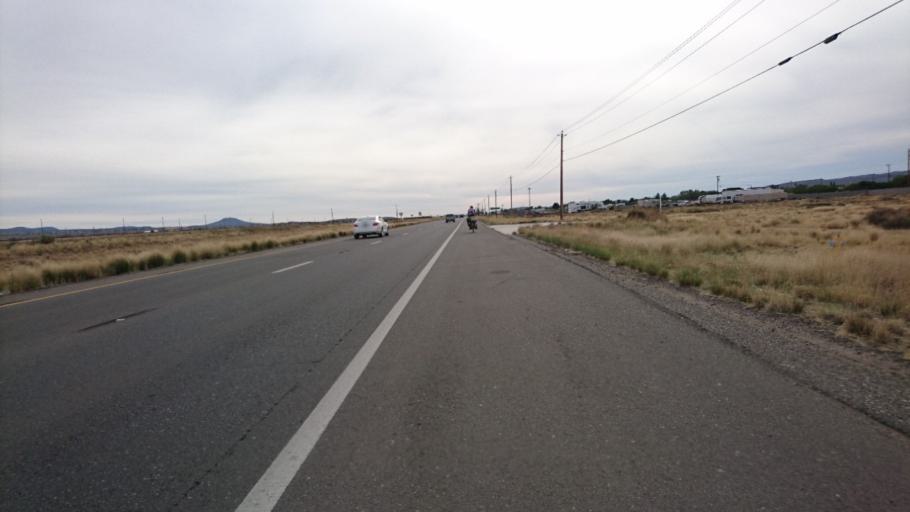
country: US
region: Arizona
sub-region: Mohave County
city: New Kingman-Butler
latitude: 35.2518
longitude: -113.9779
